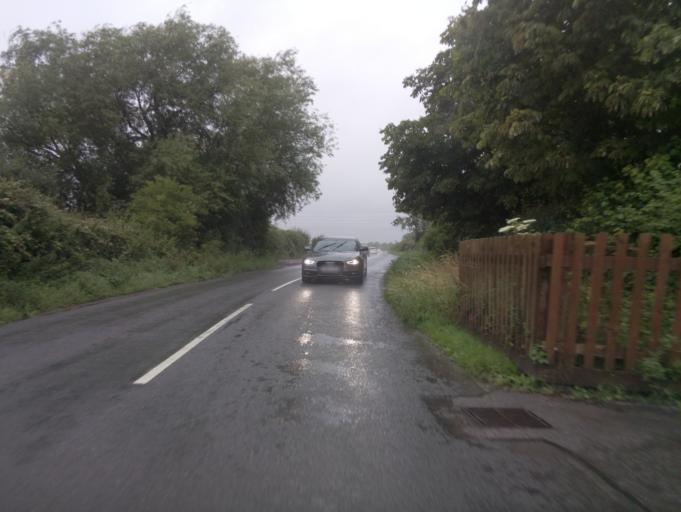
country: GB
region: England
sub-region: Gloucestershire
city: Uckington
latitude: 51.9133
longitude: -2.1428
